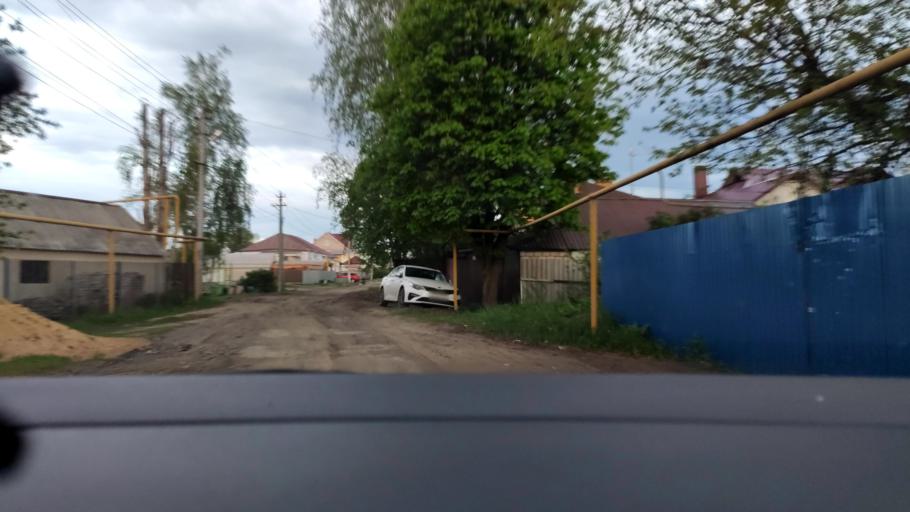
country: RU
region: Voronezj
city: Podgornoye
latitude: 51.7390
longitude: 39.1456
